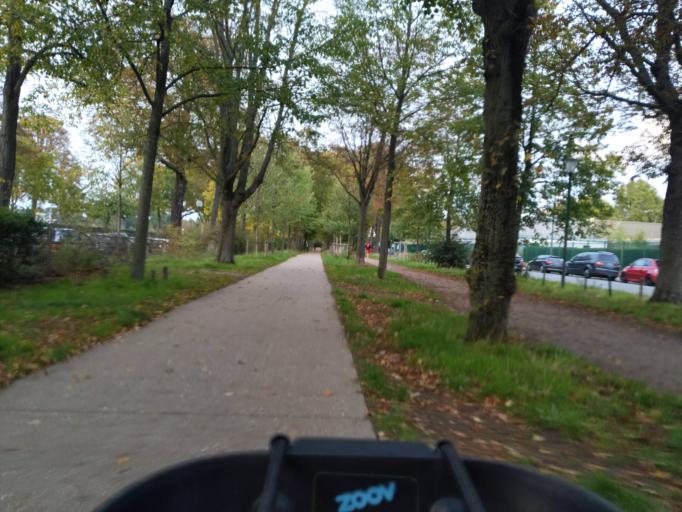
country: FR
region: Ile-de-France
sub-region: Departement des Hauts-de-Seine
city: Boulogne-Billancourt
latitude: 48.8537
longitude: 2.2608
